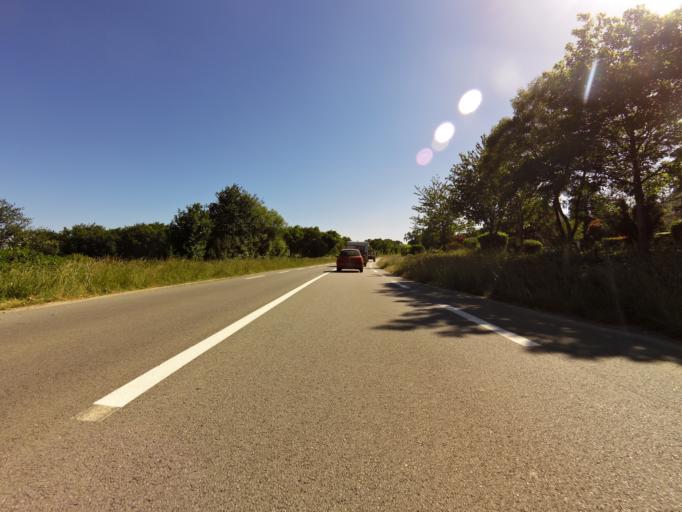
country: FR
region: Brittany
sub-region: Departement du Morbihan
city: Ferel
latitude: 47.5142
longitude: -2.3722
